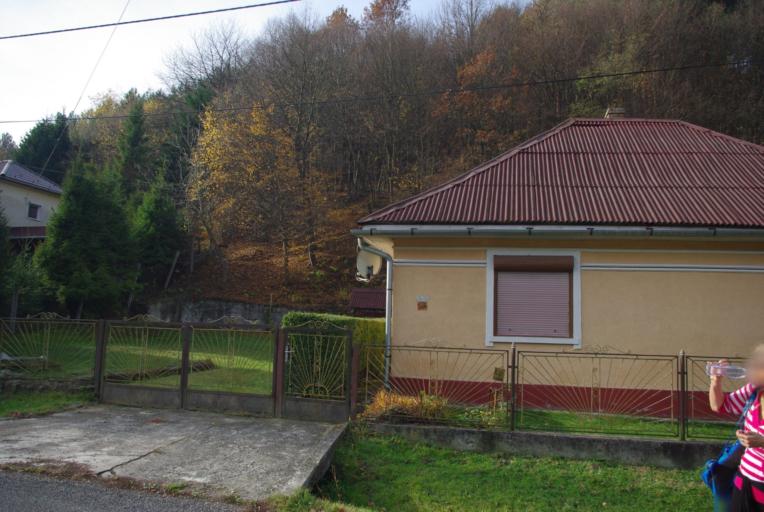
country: HU
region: Borsod-Abauj-Zemplen
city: Sarospatak
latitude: 48.4309
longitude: 21.4921
